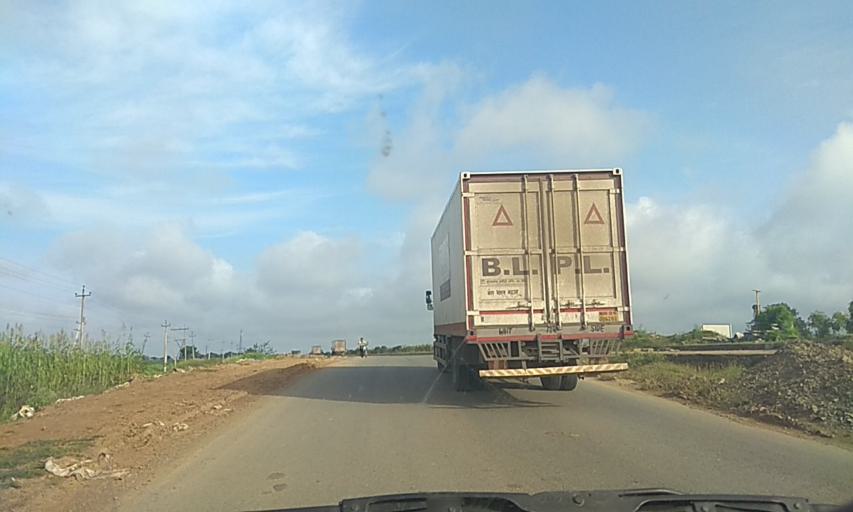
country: IN
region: Karnataka
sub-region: Haveri
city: Savanur
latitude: 14.8733
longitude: 75.3171
